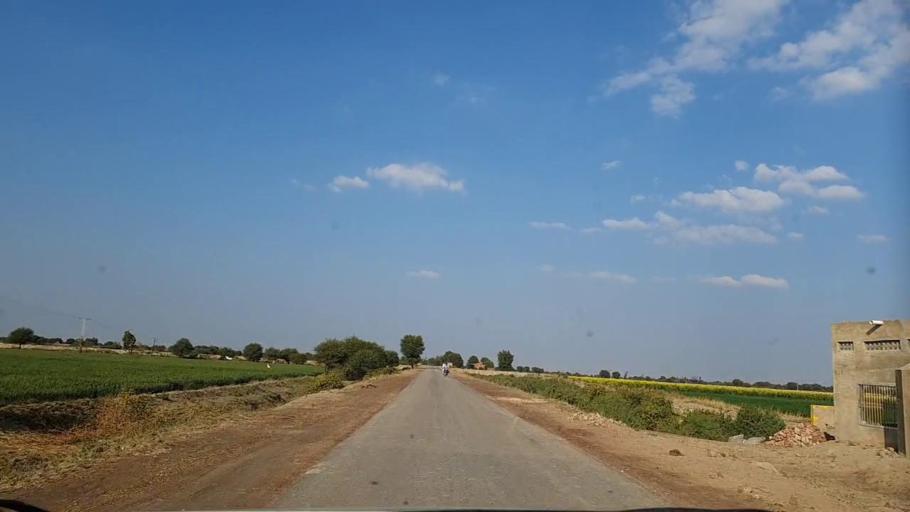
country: PK
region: Sindh
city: Pithoro
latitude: 25.6727
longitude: 69.2244
